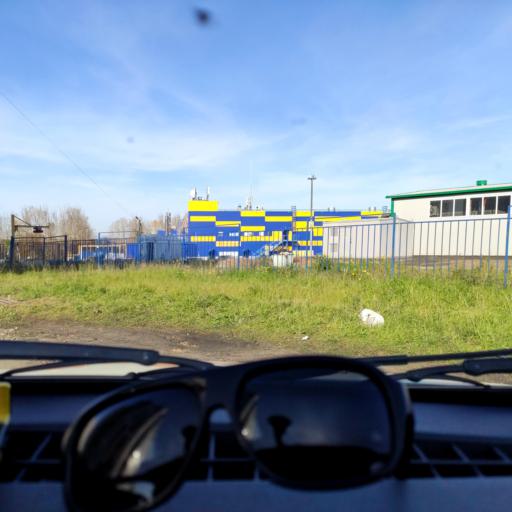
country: RU
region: Bashkortostan
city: Ufa
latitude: 54.6946
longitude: 55.9729
